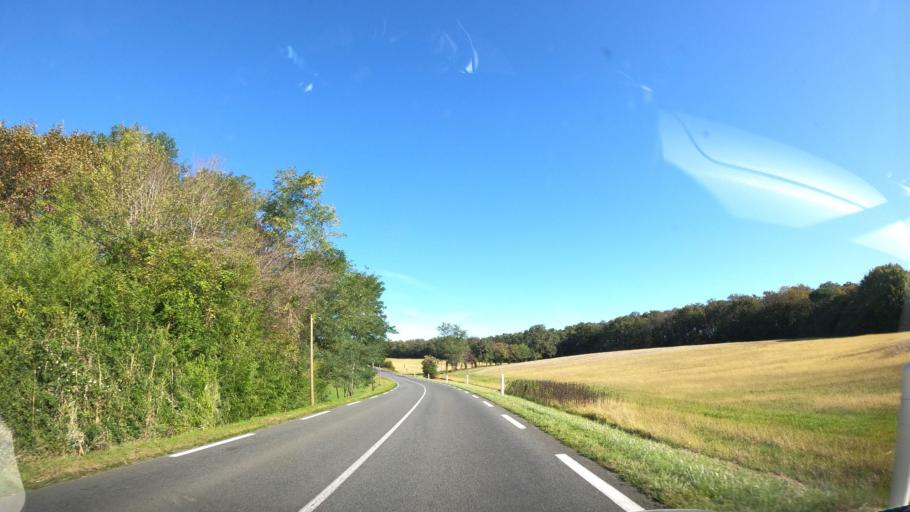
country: FR
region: Aquitaine
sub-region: Departement de la Dordogne
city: Lembras
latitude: 44.9593
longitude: 0.5881
